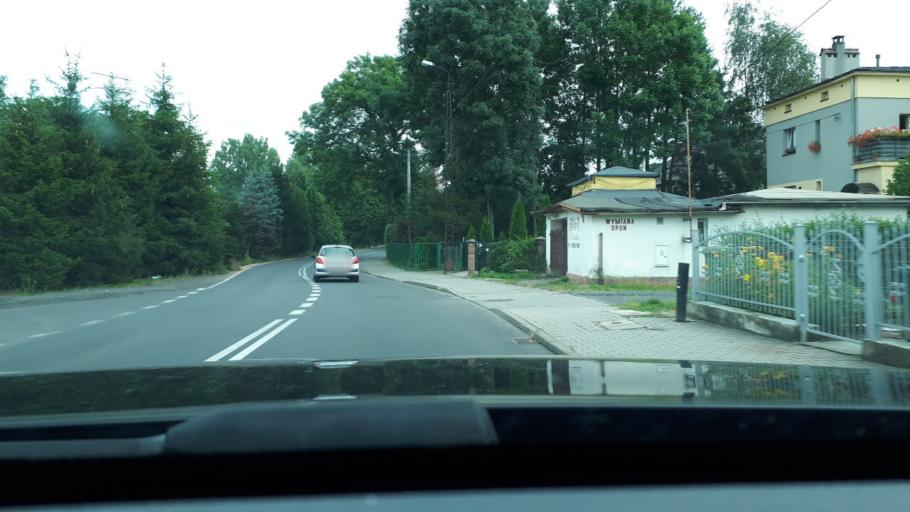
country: PL
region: Lower Silesian Voivodeship
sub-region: Powiat lubanski
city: Luban
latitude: 51.1072
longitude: 15.2915
